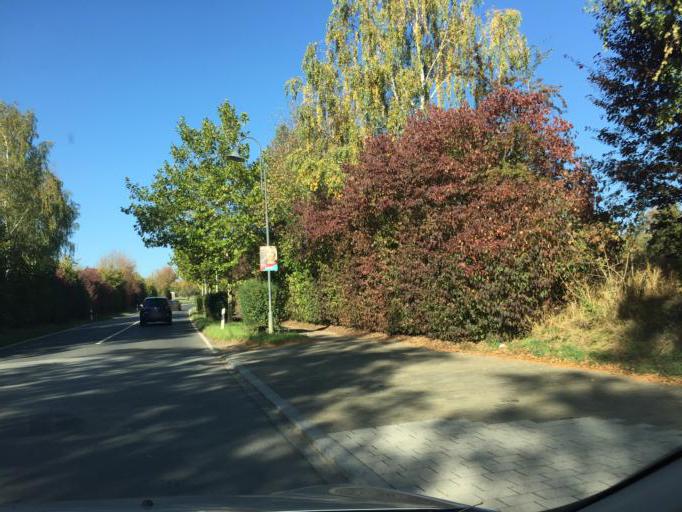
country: LU
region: Luxembourg
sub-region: Canton de Luxembourg
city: Strassen
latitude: 49.6249
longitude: 6.0639
